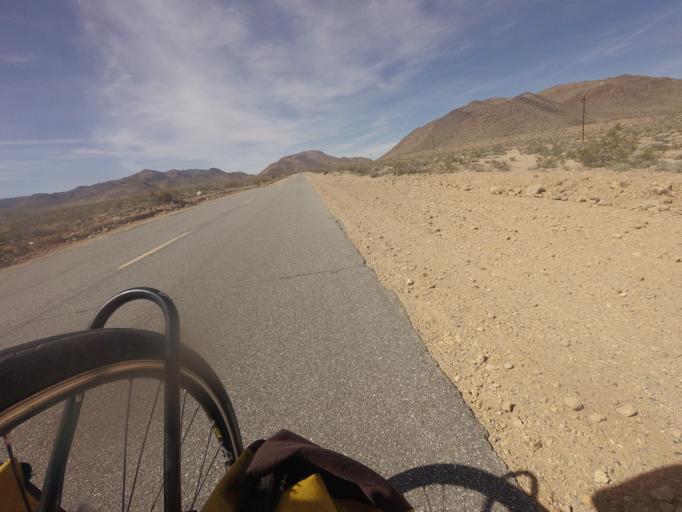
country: US
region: California
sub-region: San Bernardino County
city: Searles Valley
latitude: 35.5743
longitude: -117.4499
